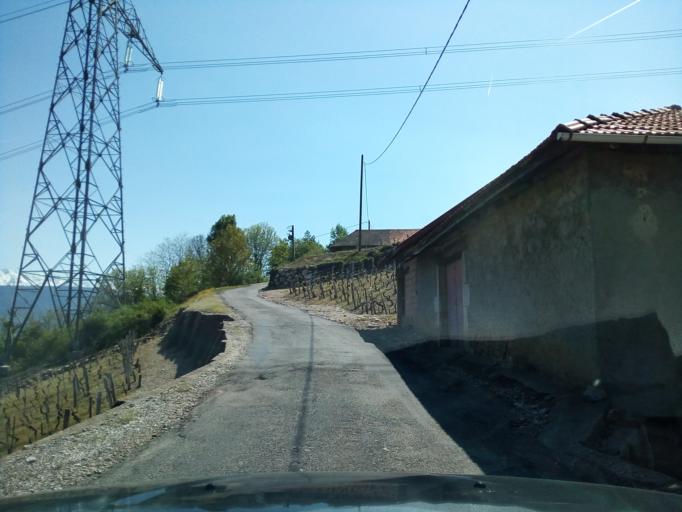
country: FR
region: Rhone-Alpes
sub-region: Departement de l'Isere
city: Chapareillan
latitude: 45.4839
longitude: 5.9777
